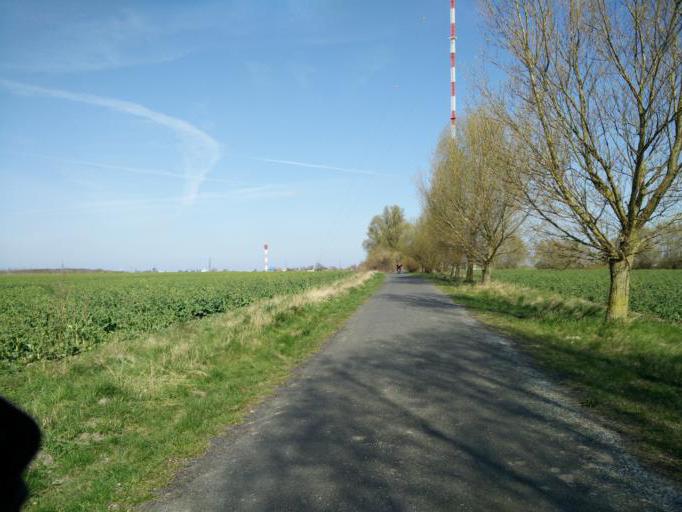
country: DE
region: Mecklenburg-Vorpommern
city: Dierkow-West
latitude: 54.1265
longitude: 12.1291
